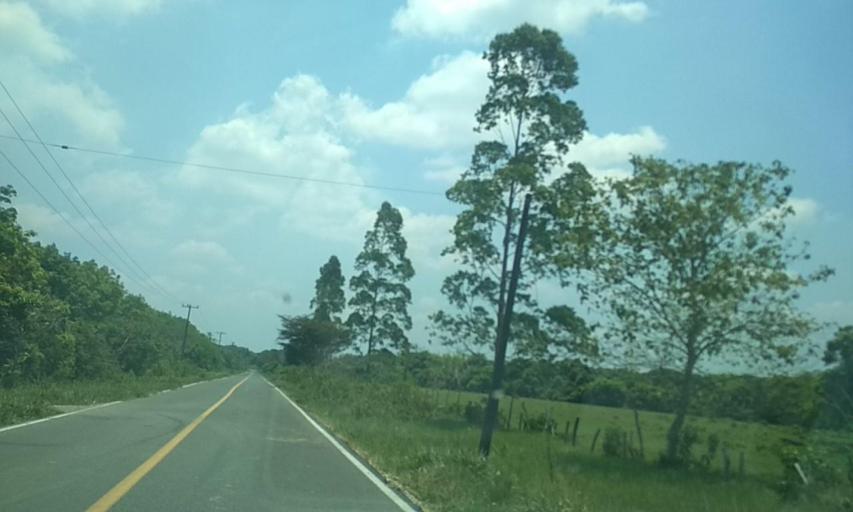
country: MX
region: Tabasco
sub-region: Huimanguillo
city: Francisco Rueda
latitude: 17.7546
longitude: -94.0485
